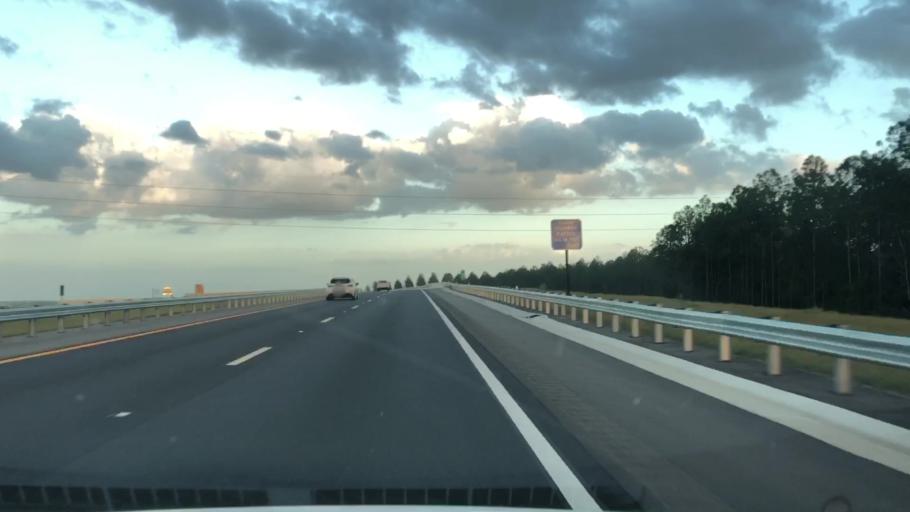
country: US
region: Florida
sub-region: Lake County
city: Mount Plymouth
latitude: 28.7759
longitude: -81.5335
